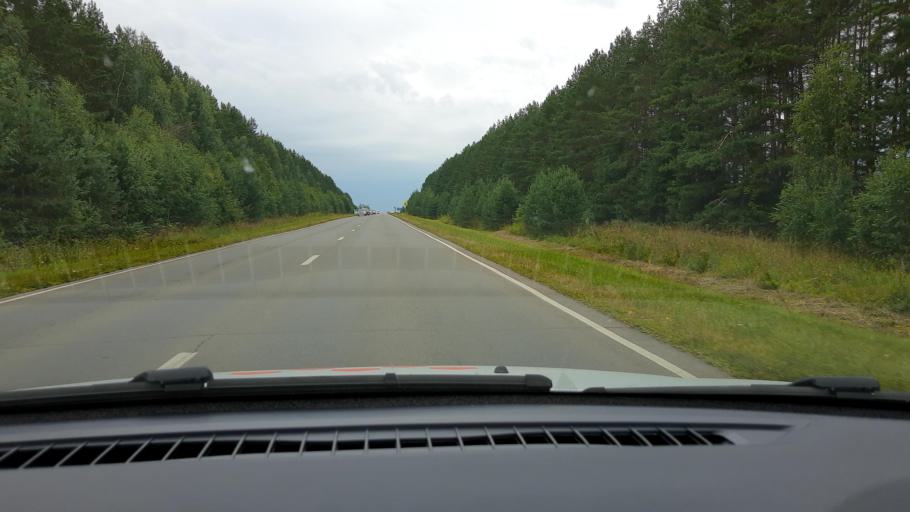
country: RU
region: Nizjnij Novgorod
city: Vyyezdnoye
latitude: 55.1584
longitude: 43.5793
